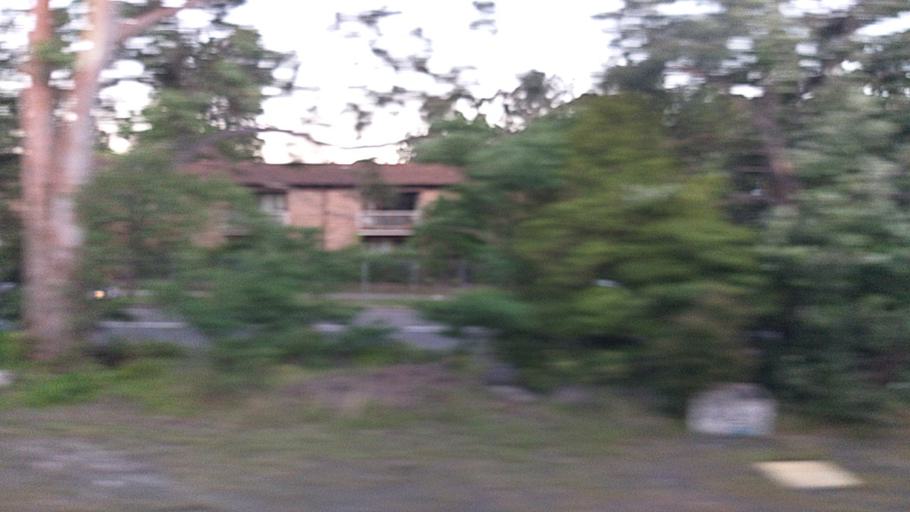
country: AU
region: New South Wales
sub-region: Sutherland Shire
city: Heathcote
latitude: -34.0813
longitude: 151.0116
